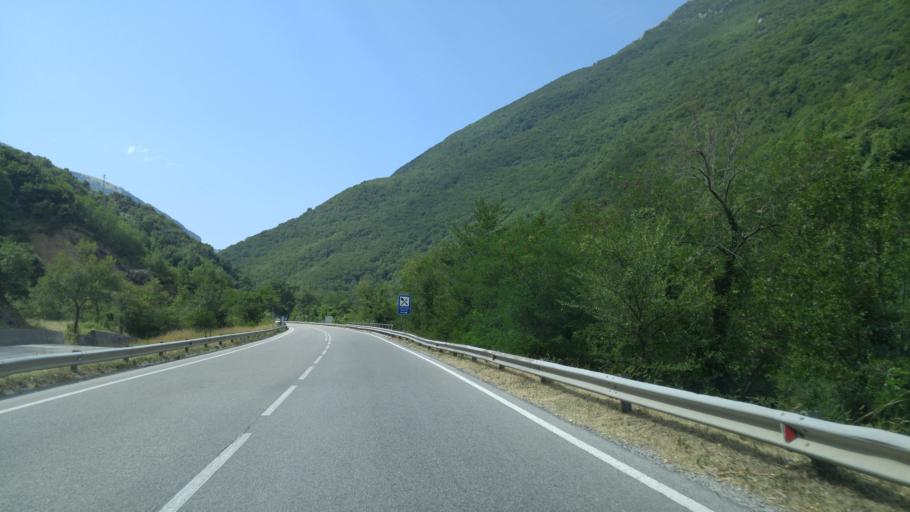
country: IT
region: The Marches
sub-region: Provincia di Pesaro e Urbino
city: Cagli
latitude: 43.5189
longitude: 12.6414
